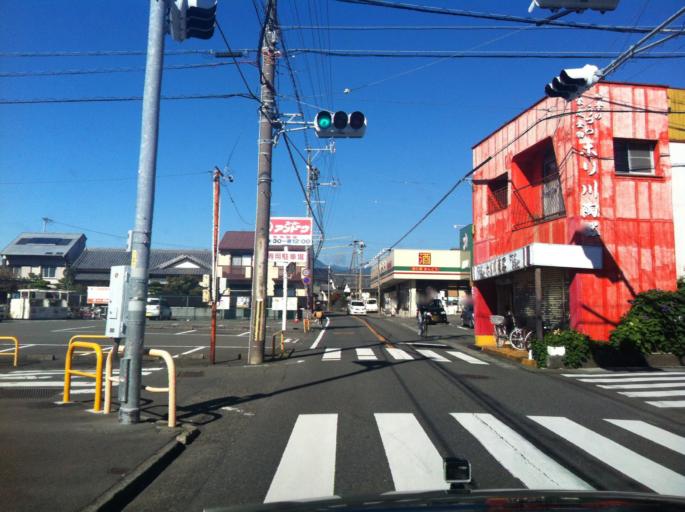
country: JP
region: Shizuoka
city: Shizuoka-shi
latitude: 34.9794
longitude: 138.4258
